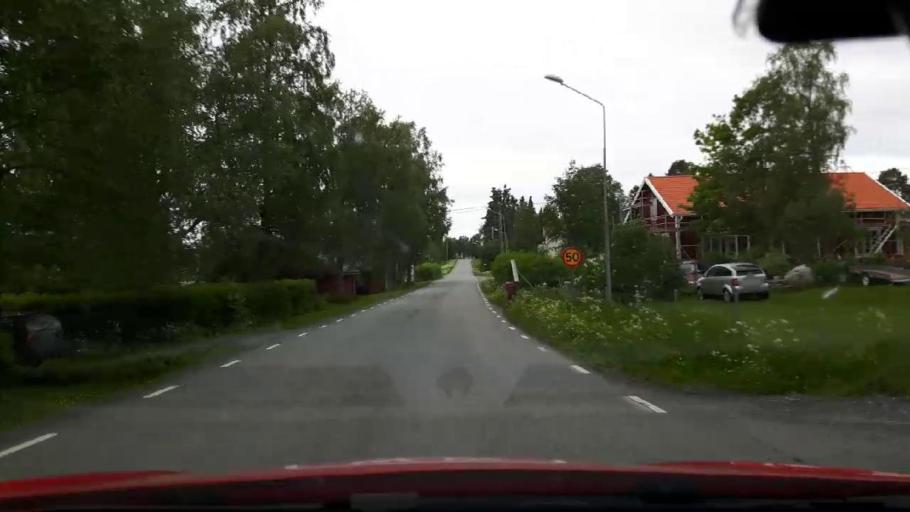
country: SE
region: Jaemtland
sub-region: OEstersunds Kommun
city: Ostersund
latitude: 63.2503
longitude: 14.5418
